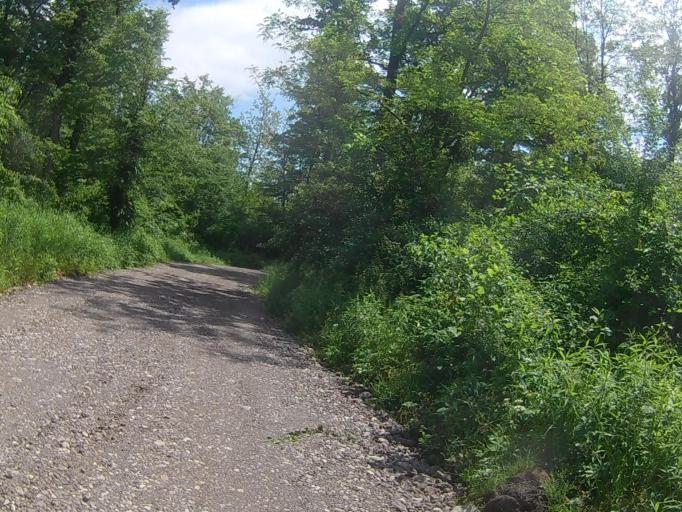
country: SI
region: Starse
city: Starse
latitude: 46.4810
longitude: 15.7604
